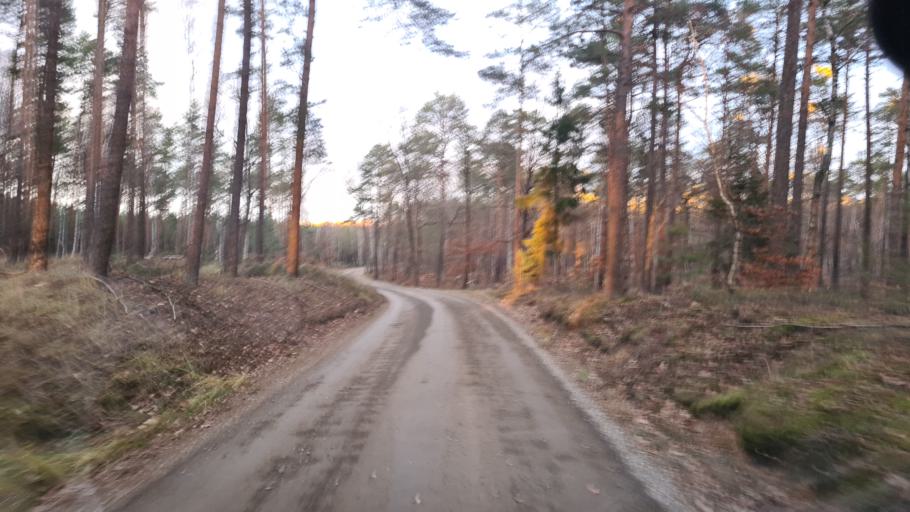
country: DE
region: Brandenburg
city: Schonborn
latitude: 51.5826
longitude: 13.4825
